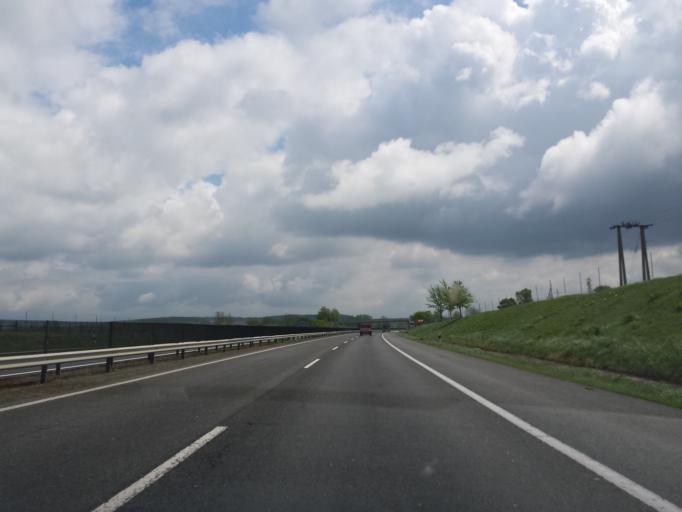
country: HU
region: Komarom-Esztergom
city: Mocsa
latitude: 47.6591
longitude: 18.1836
